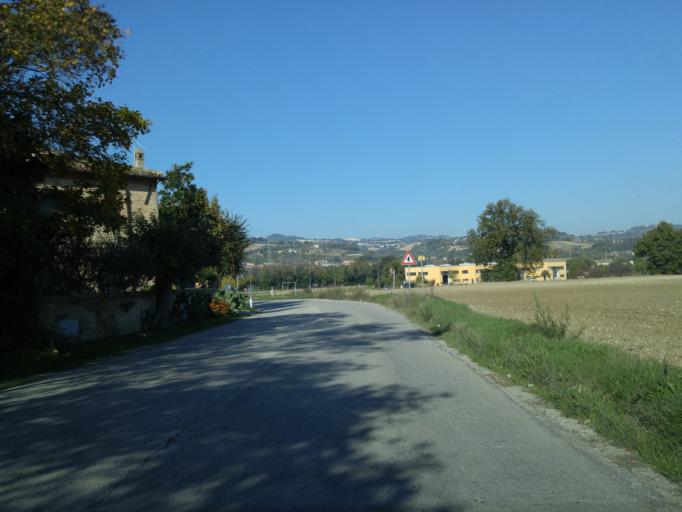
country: IT
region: The Marches
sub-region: Provincia di Pesaro e Urbino
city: Tavernelle
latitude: 43.7220
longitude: 12.8949
